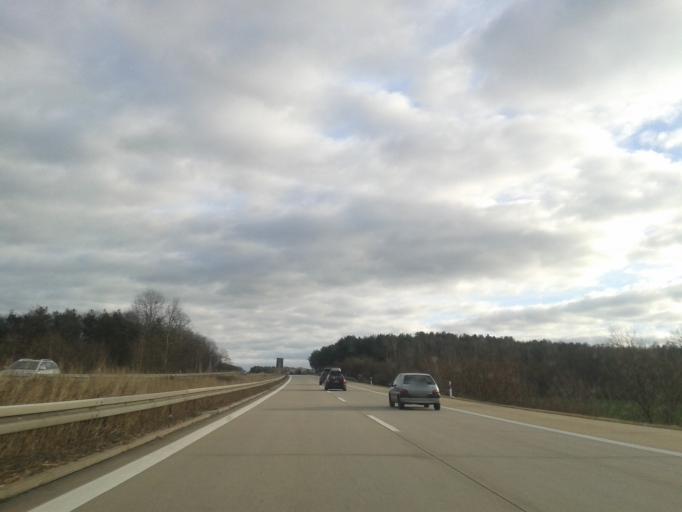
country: DE
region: Saxony
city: Guttau
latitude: 51.2102
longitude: 14.5776
